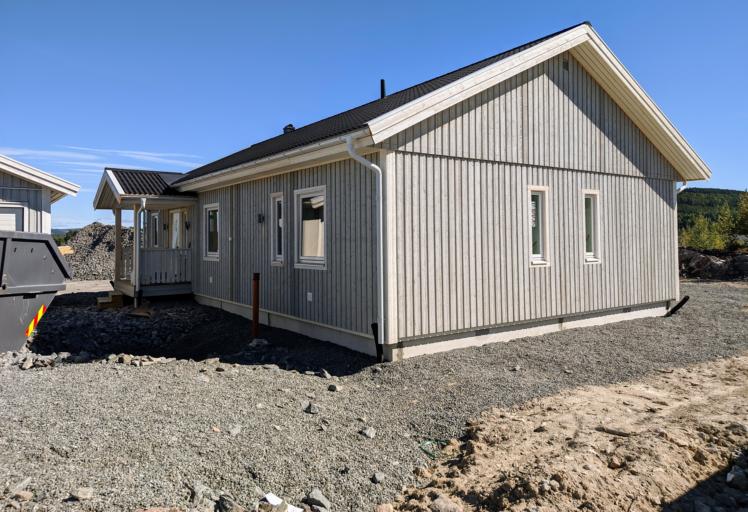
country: NO
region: Akershus
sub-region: Nes
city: Arnes
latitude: 60.1735
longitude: 11.5485
